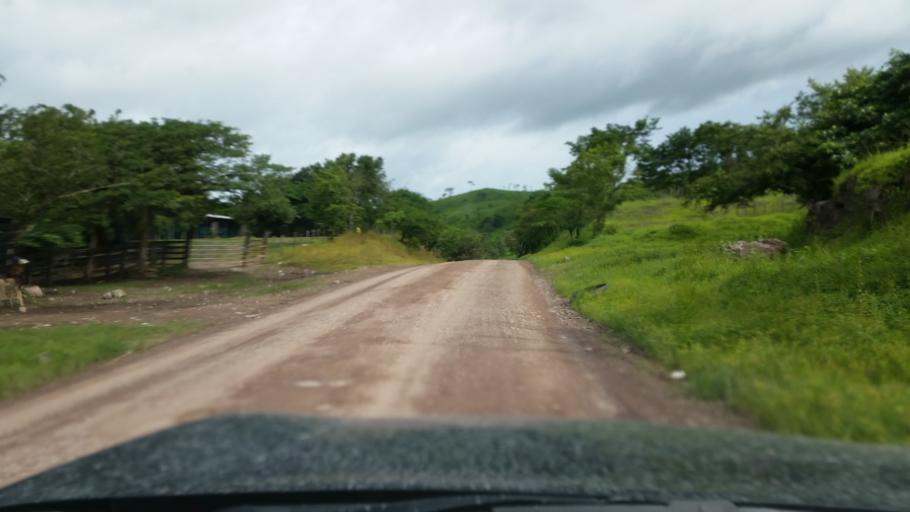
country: NI
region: Atlantico Norte (RAAN)
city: Siuna
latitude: 13.5303
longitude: -84.8233
